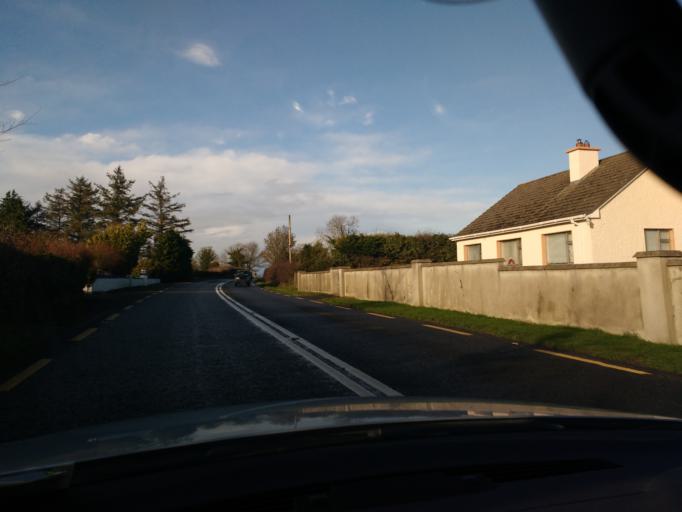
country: IE
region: Munster
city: Thurles
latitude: 52.6420
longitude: -7.7877
